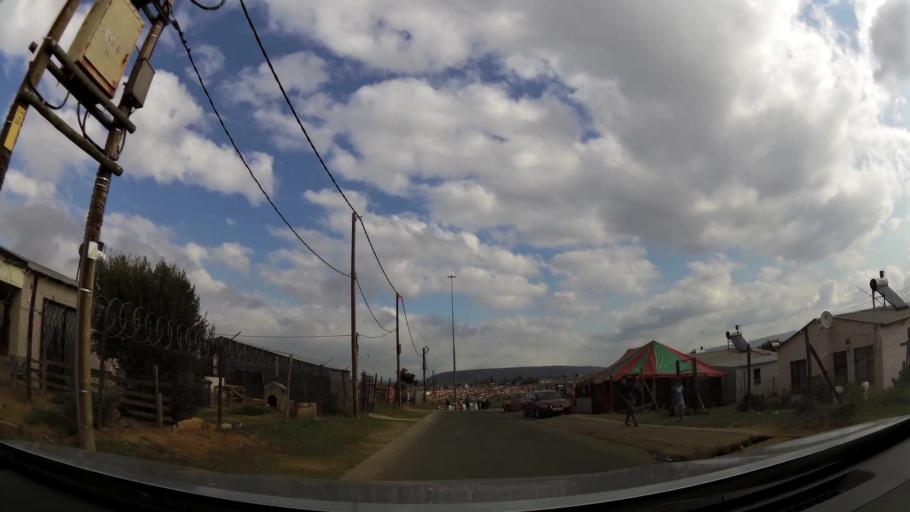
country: ZA
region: Eastern Cape
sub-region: Nelson Mandela Bay Metropolitan Municipality
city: Uitenhage
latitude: -33.7477
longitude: 25.3930
